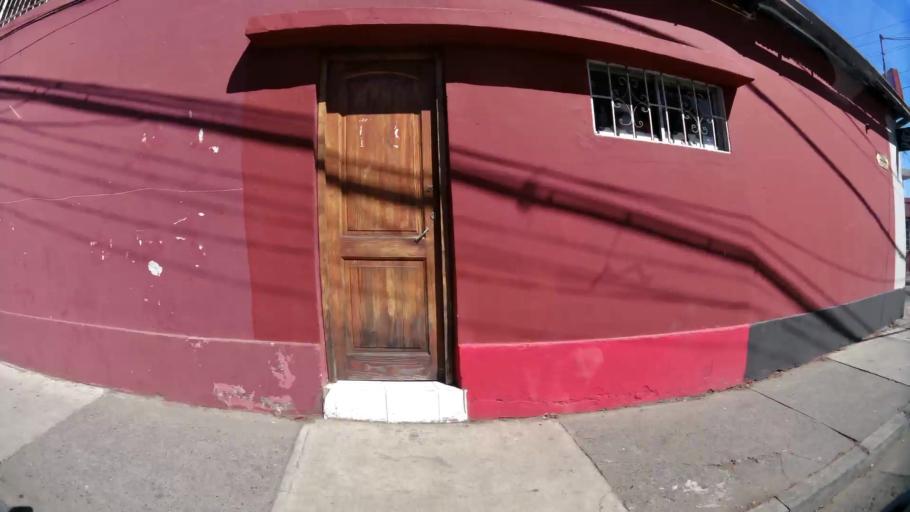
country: CL
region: O'Higgins
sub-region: Provincia de Cachapoal
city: Rancagua
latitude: -34.1766
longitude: -70.7482
